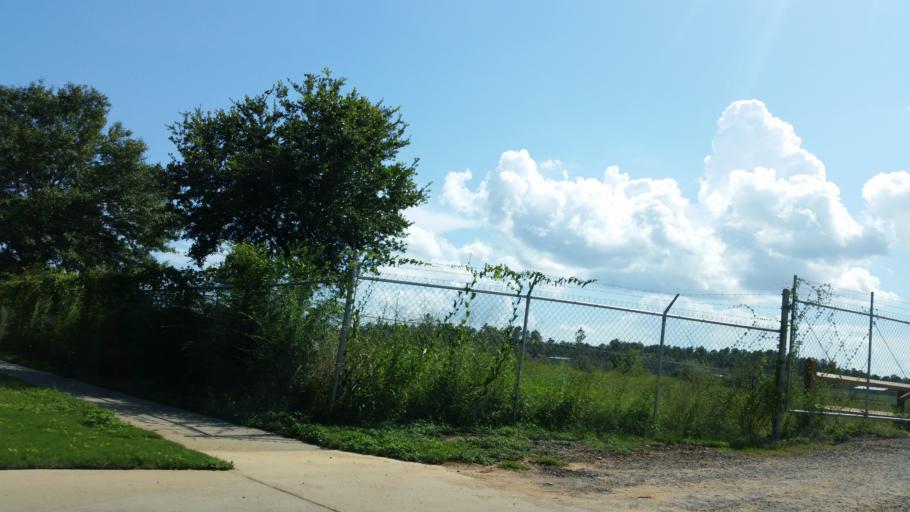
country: US
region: Florida
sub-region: Escambia County
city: Ensley
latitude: 30.5304
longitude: -87.2499
